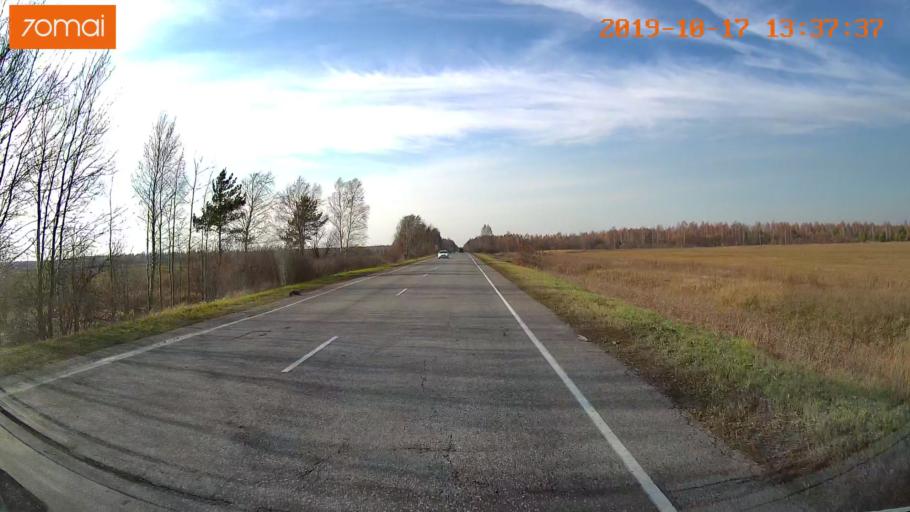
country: RU
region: Rjazan
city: Tuma
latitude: 55.1420
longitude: 40.6343
